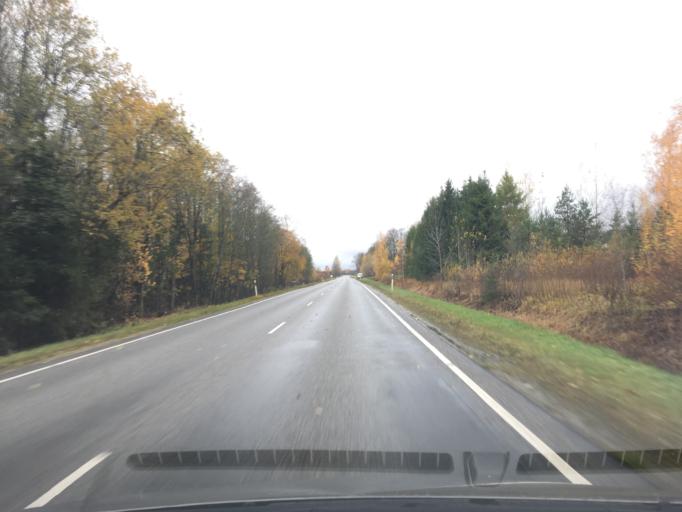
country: EE
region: Jogevamaa
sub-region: Tabivere vald
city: Tabivere
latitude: 58.4656
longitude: 26.5697
